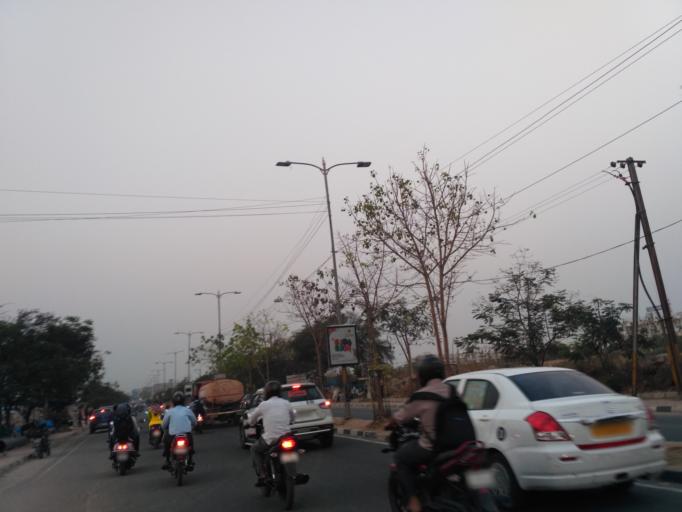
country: IN
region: Telangana
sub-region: Rangareddi
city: Kukatpalli
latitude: 17.4467
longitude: 78.3948
